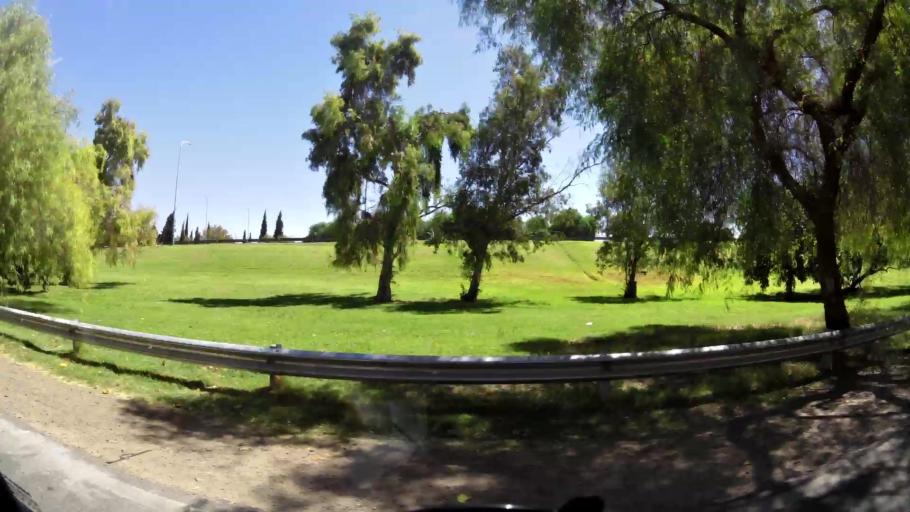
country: AR
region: San Juan
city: San Juan
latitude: -31.5201
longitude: -68.5344
